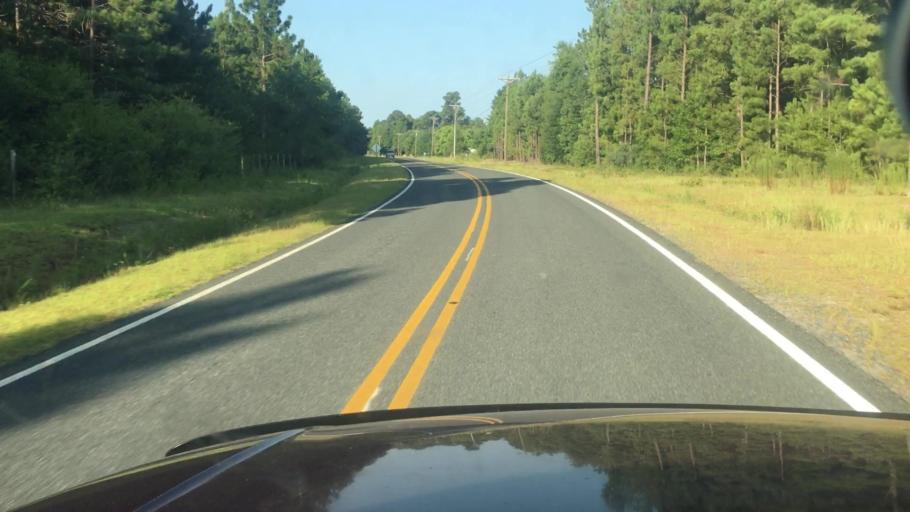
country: US
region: North Carolina
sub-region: Robeson County
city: Saint Pauls
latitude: 34.8544
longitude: -78.8523
